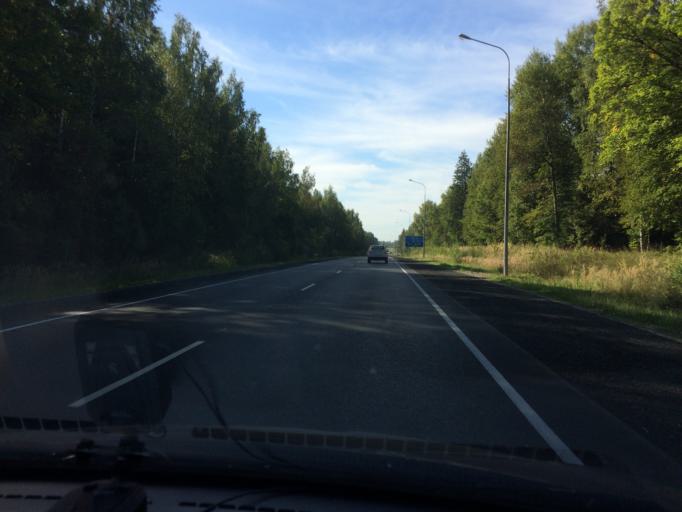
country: RU
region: Mariy-El
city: Yoshkar-Ola
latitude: 56.5894
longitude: 47.9738
